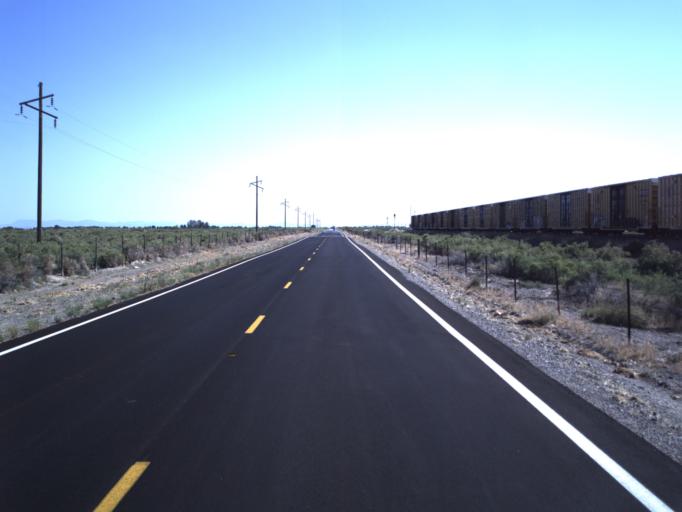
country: US
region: Utah
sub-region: Millard County
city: Delta
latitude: 39.2392
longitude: -112.6636
